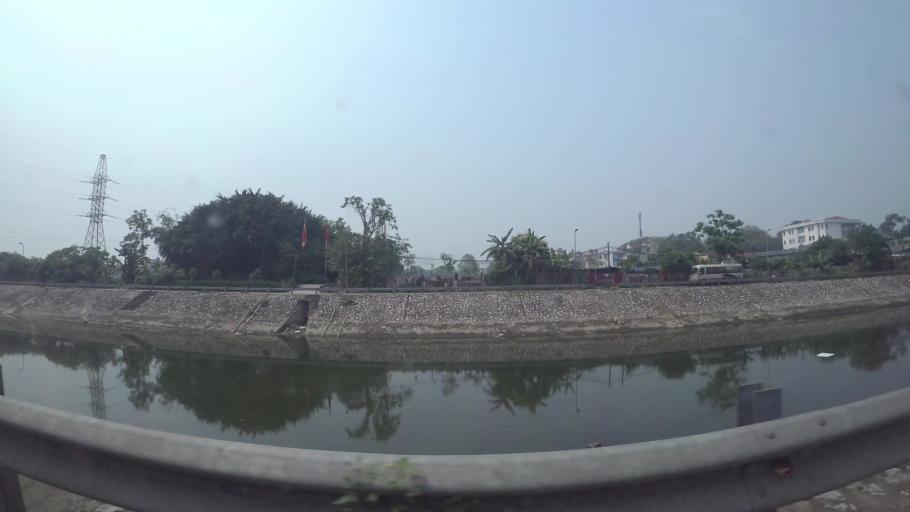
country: VN
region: Ha Noi
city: Van Dien
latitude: 20.9572
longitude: 105.8239
